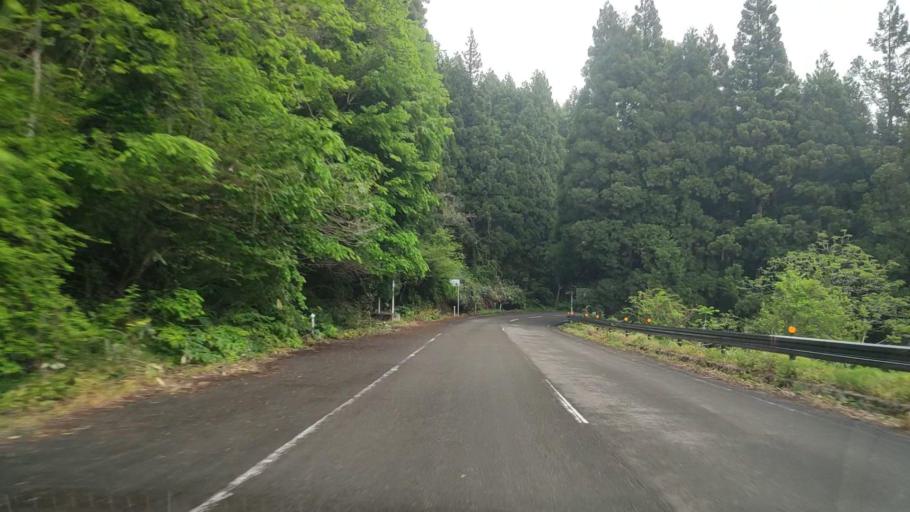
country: JP
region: Niigata
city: Kamo
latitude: 37.7108
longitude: 139.0942
